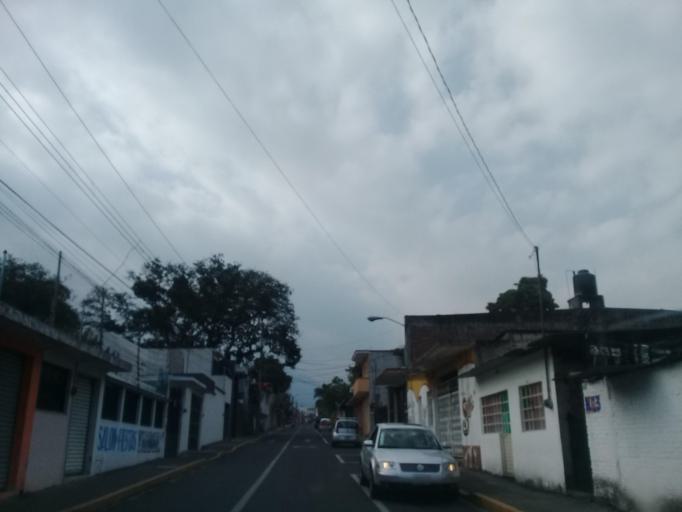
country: MX
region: Veracruz
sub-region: Ixhuatlancillo
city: Union y Progreso
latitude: 18.8699
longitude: -97.1061
